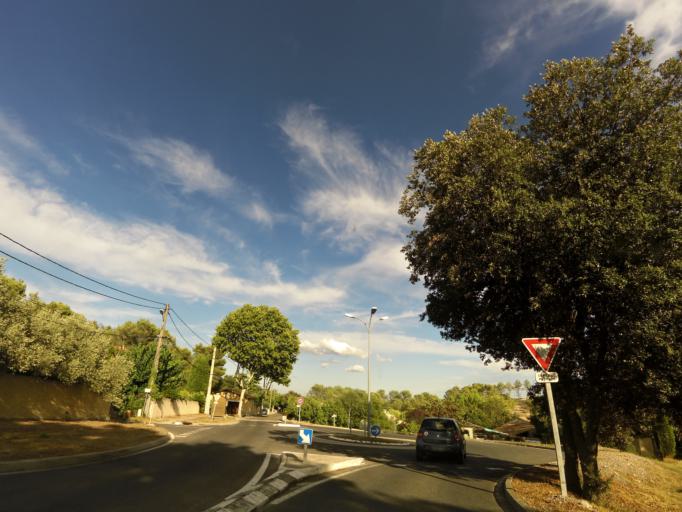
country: FR
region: Languedoc-Roussillon
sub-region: Departement de l'Herault
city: Saint-Drezery
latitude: 43.7698
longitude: 3.9498
